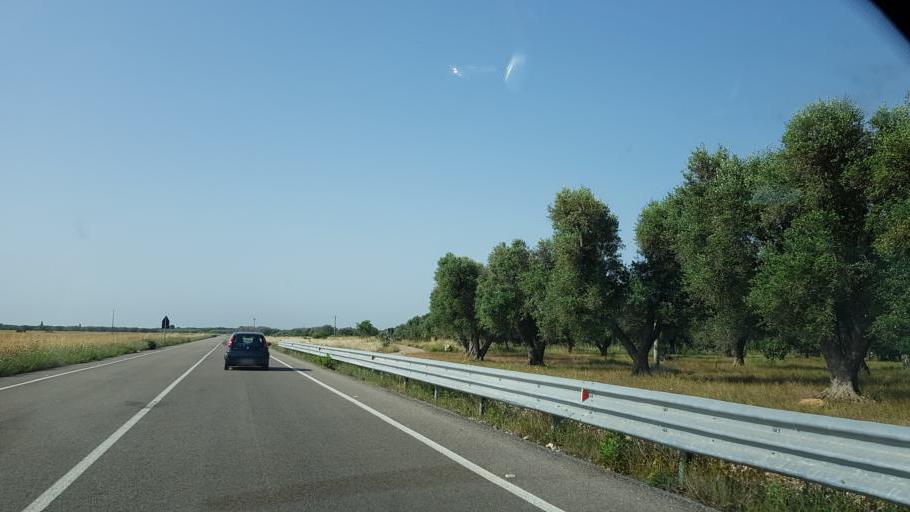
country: IT
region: Apulia
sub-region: Provincia di Brindisi
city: Mesagne
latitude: 40.5044
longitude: 17.8278
